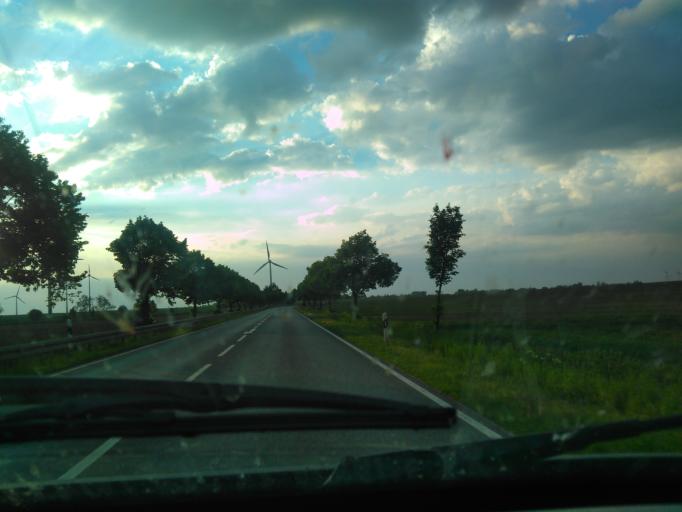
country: DE
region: Saxony-Anhalt
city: Osterfeld
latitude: 51.0984
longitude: 11.9409
